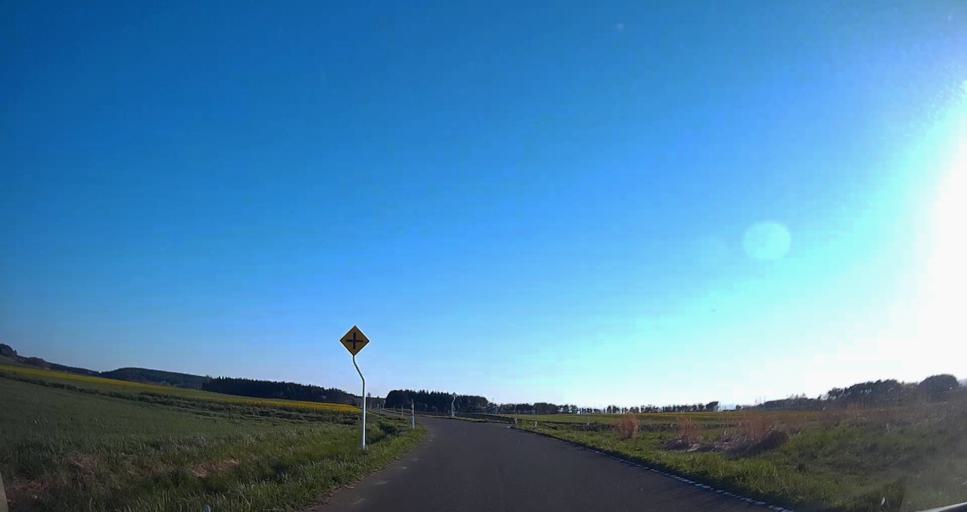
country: JP
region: Aomori
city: Mutsu
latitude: 41.1166
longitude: 141.2747
